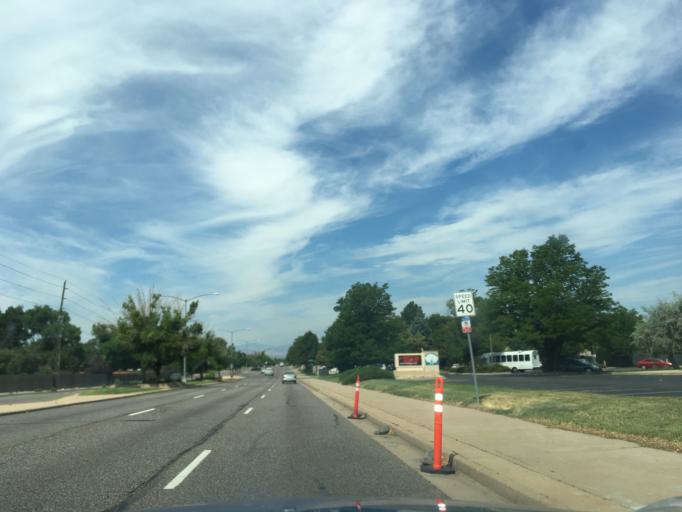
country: US
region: Colorado
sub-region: Adams County
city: Aurora
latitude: 39.7113
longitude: -104.8550
